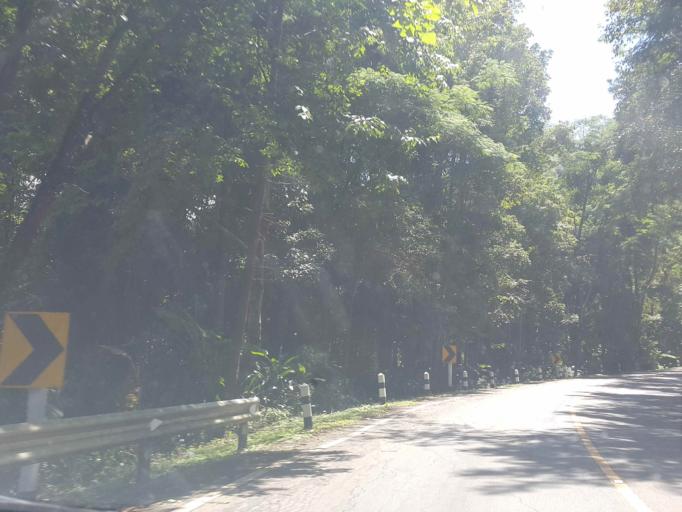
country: TH
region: Chiang Mai
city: Mae Chaem
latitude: 18.5442
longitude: 98.5334
